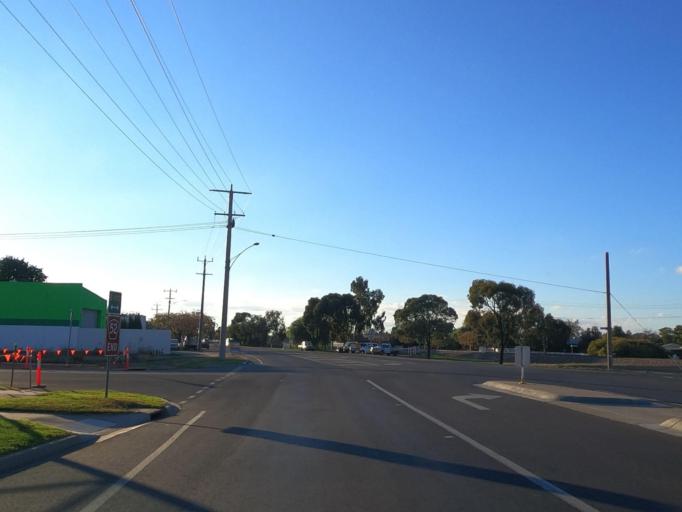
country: AU
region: Victoria
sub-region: Swan Hill
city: Swan Hill
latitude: -35.3349
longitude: 143.5598
